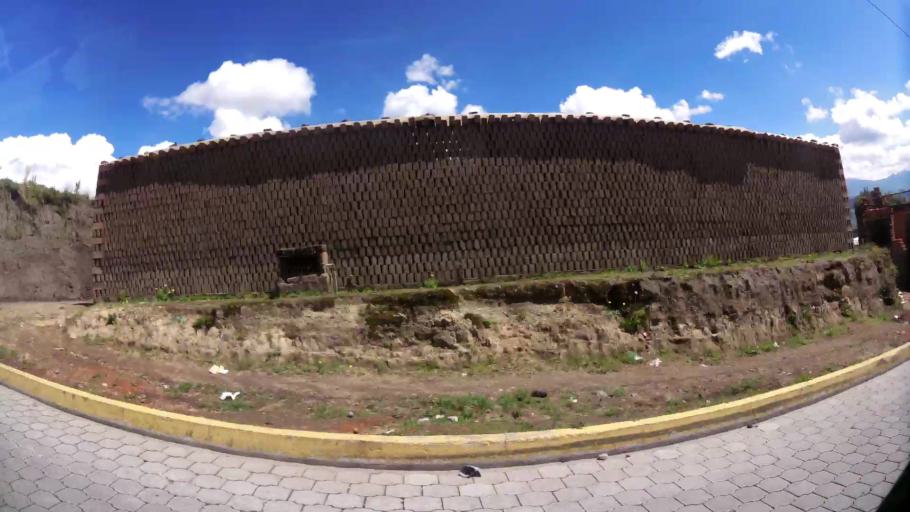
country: EC
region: Pichincha
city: Quito
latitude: -0.3260
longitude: -78.5665
